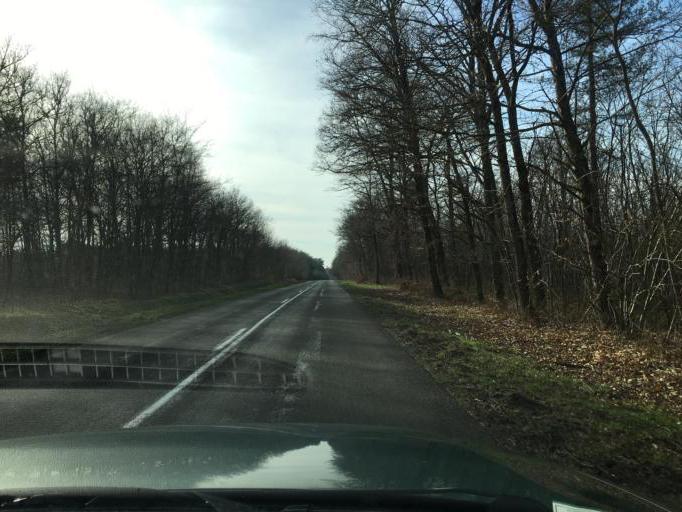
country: FR
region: Centre
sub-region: Departement du Loiret
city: Ligny-le-Ribault
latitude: 47.6859
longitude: 1.8015
